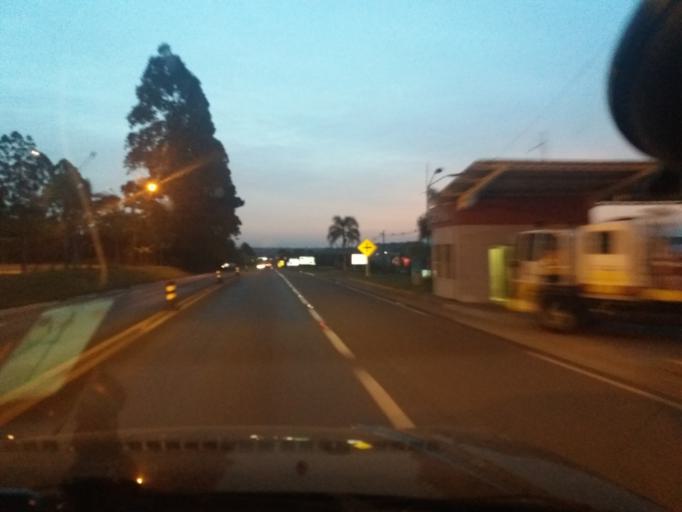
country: BR
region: Sao Paulo
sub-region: Itapeva
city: Itapeva
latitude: -23.9735
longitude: -48.8597
